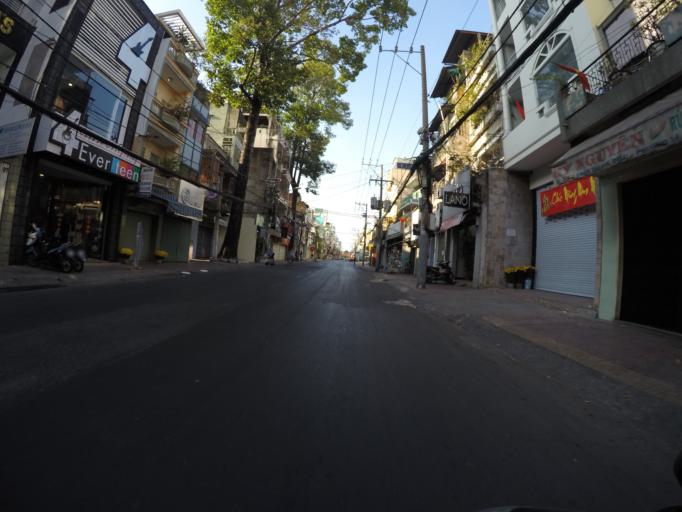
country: VN
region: Ho Chi Minh City
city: Quan Phu Nhuan
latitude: 10.7903
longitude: 106.6781
